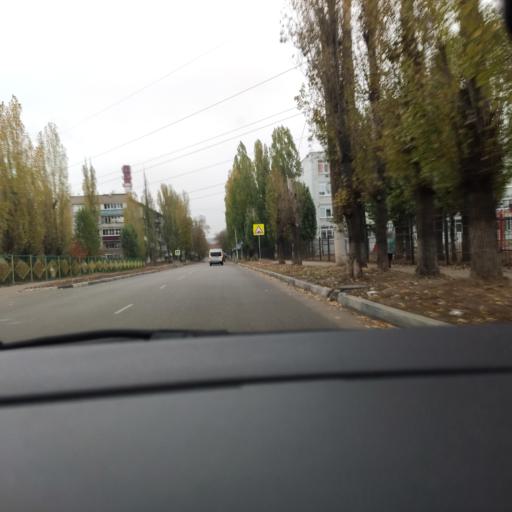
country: RU
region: Voronezj
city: Pridonskoy
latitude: 51.6569
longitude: 39.1103
